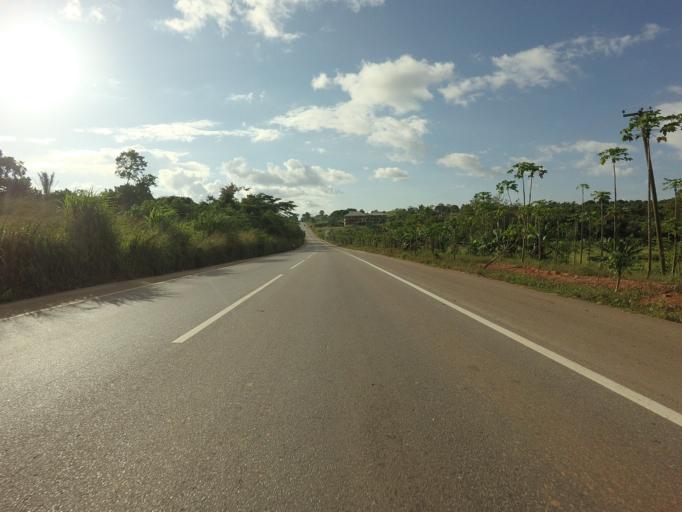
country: GH
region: Ashanti
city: Tafo
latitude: 6.8843
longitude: -1.6446
